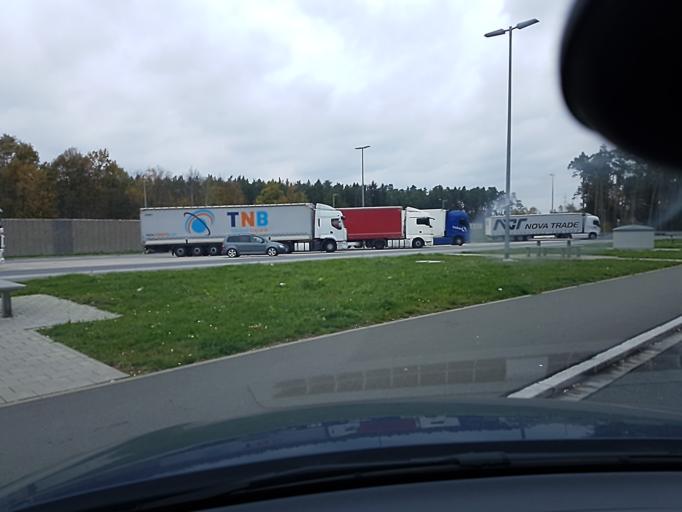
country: DE
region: Bavaria
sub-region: Regierungsbezirk Mittelfranken
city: Heilsbronn
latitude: 49.3085
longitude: 10.8269
